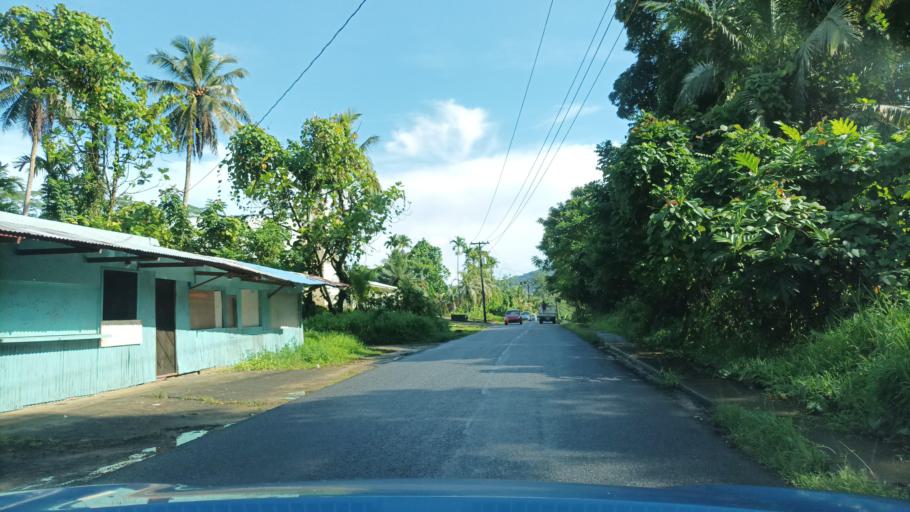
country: FM
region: Pohnpei
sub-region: Sokehs Municipality
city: Palikir - National Government Center
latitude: 6.9327
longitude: 158.1807
